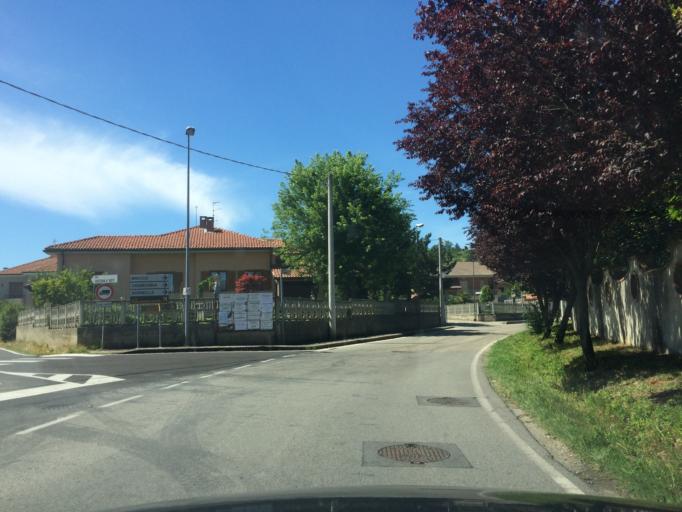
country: IT
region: Piedmont
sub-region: Provincia di Asti
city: Nizza Monferrato
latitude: 44.7769
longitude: 8.3488
